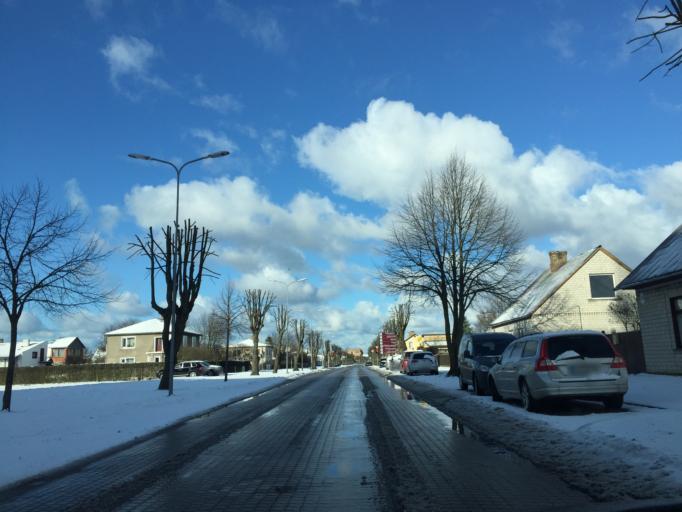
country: LV
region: Ventspils
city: Ventspils
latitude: 57.3821
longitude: 21.5539
